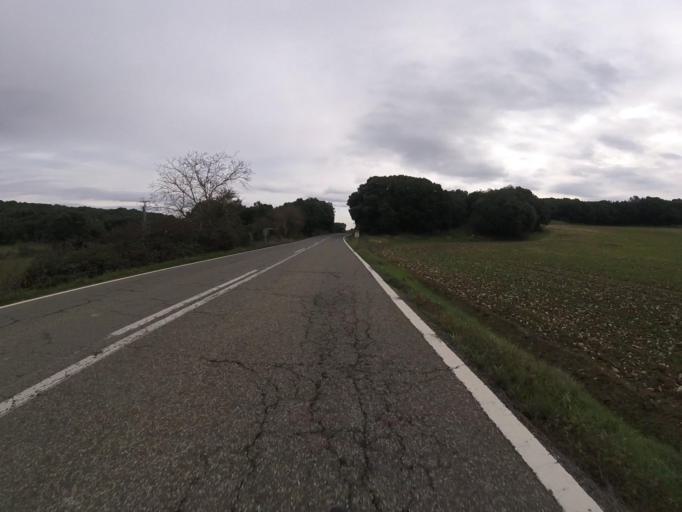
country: ES
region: Navarre
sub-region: Provincia de Navarra
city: Lezaun
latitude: 42.7387
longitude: -2.0177
